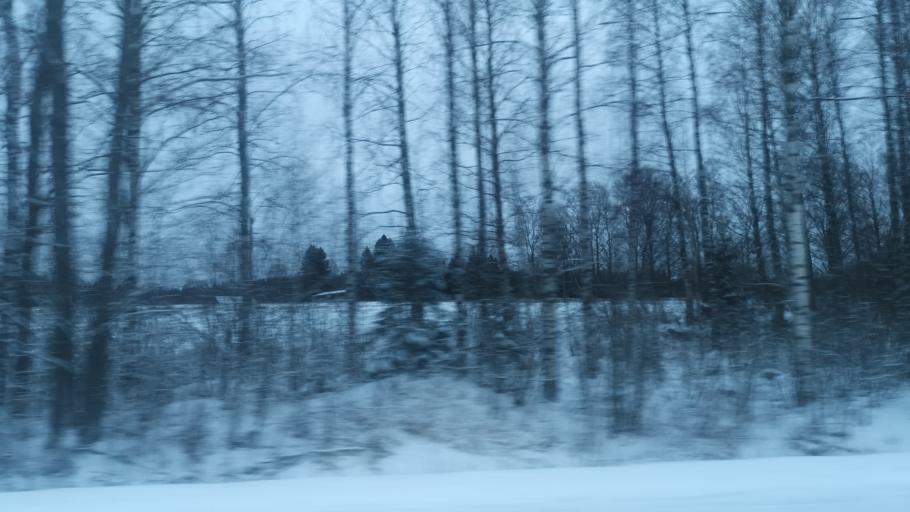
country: FI
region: Southern Savonia
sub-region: Savonlinna
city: Savonlinna
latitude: 62.0002
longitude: 28.7449
